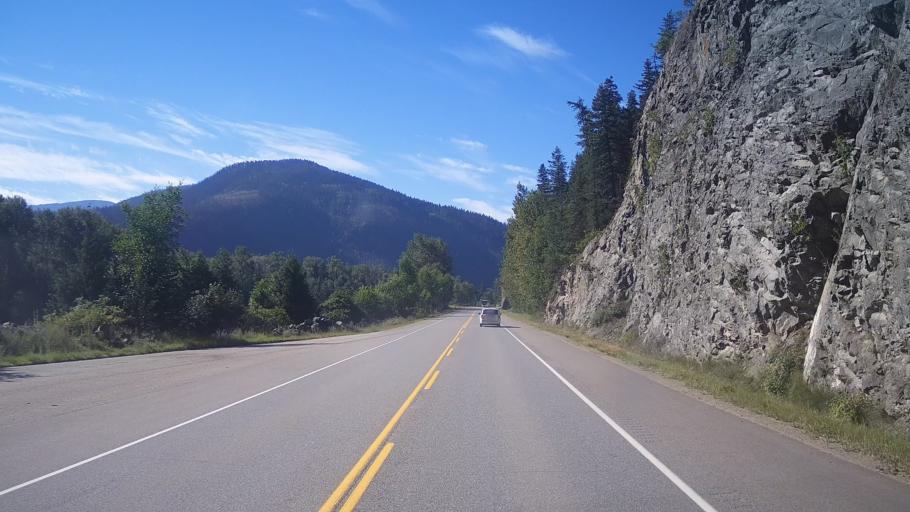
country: CA
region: British Columbia
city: Kamloops
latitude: 51.4691
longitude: -120.1781
